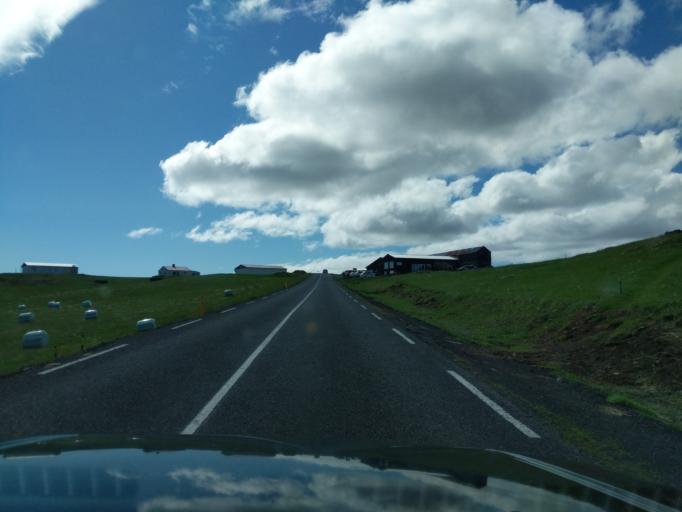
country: IS
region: West
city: Olafsvik
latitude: 64.7506
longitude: -23.6492
